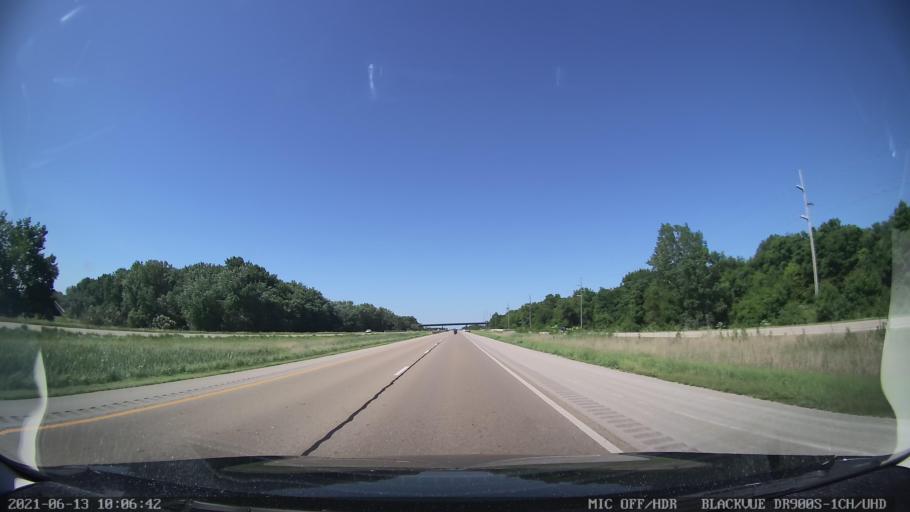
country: US
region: Illinois
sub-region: Logan County
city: Atlanta
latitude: 40.2245
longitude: -89.2739
